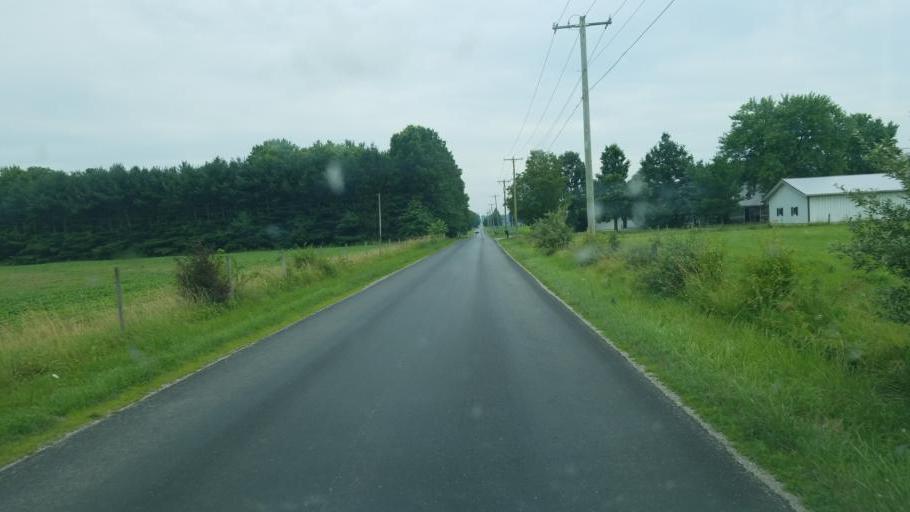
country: US
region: Ohio
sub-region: Wayne County
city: Orrville
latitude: 40.8108
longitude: -81.7750
